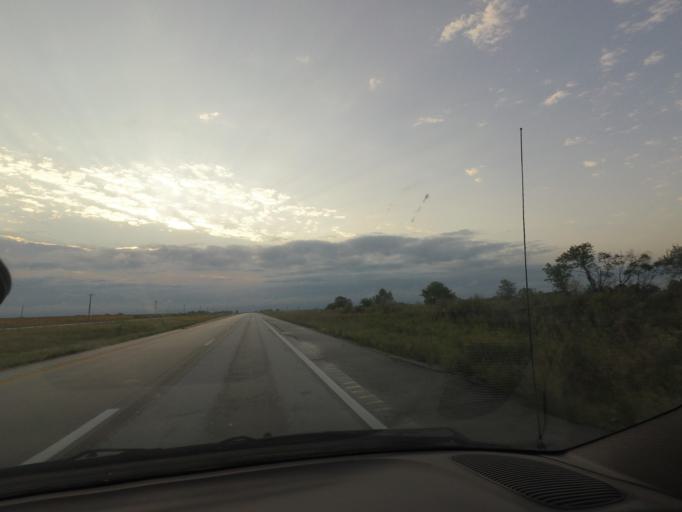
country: US
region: Missouri
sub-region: Shelby County
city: Shelbina
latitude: 39.7150
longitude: -92.1313
